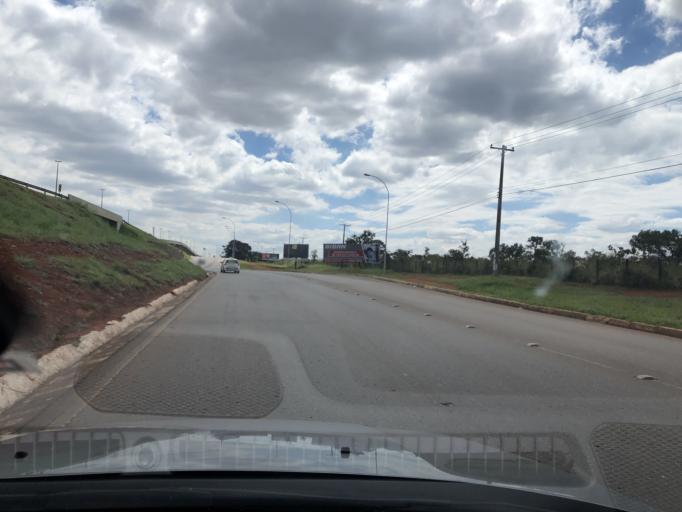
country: BR
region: Federal District
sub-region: Brasilia
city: Brasilia
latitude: -16.0033
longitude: -47.9837
